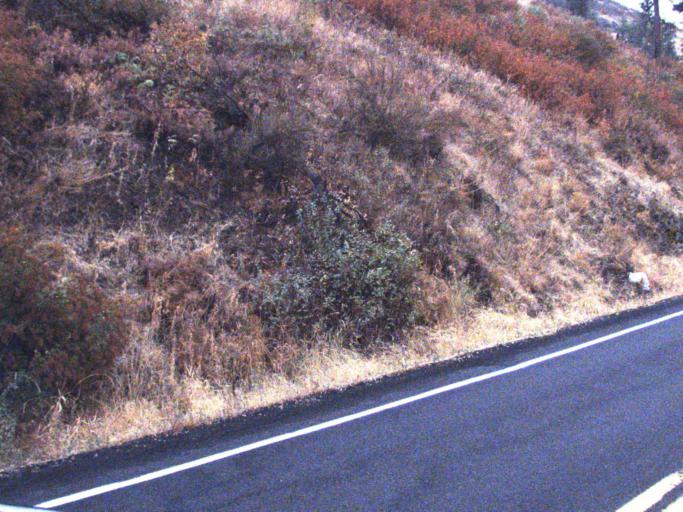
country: US
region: Washington
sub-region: Spokane County
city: Medical Lake
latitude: 47.7530
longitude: -117.8891
